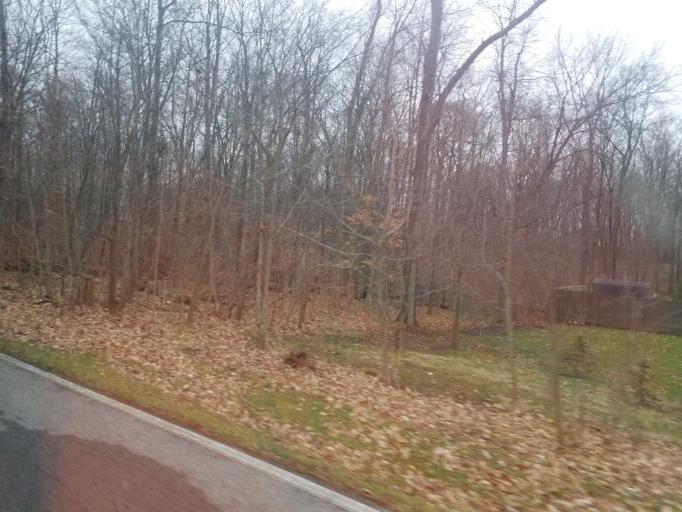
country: US
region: Ohio
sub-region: Franklin County
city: Westerville
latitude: 40.1902
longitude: -82.9302
